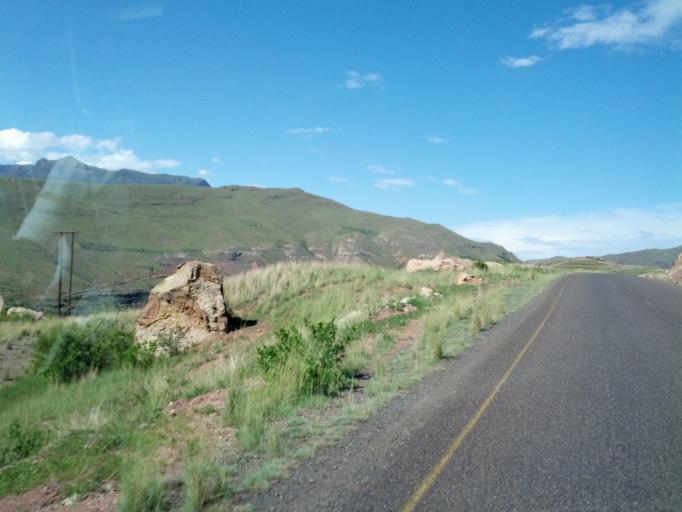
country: LS
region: Qacha's Nek
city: Qacha's Nek
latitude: -30.0631
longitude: 28.5246
